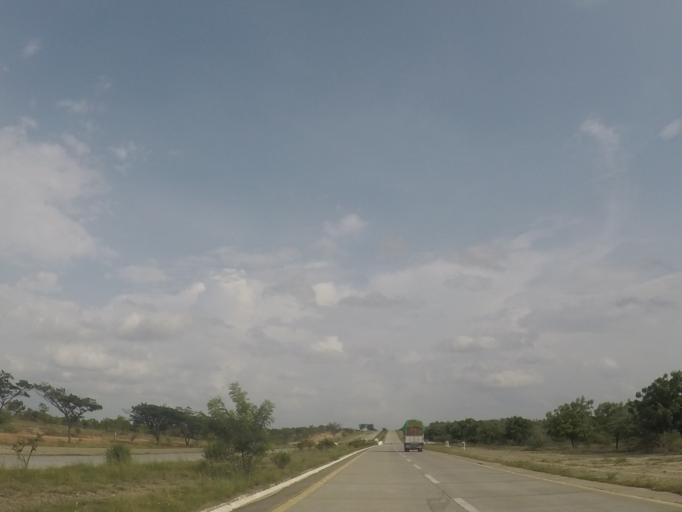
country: MM
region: Mandalay
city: Meiktila
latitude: 20.6759
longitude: 95.7973
